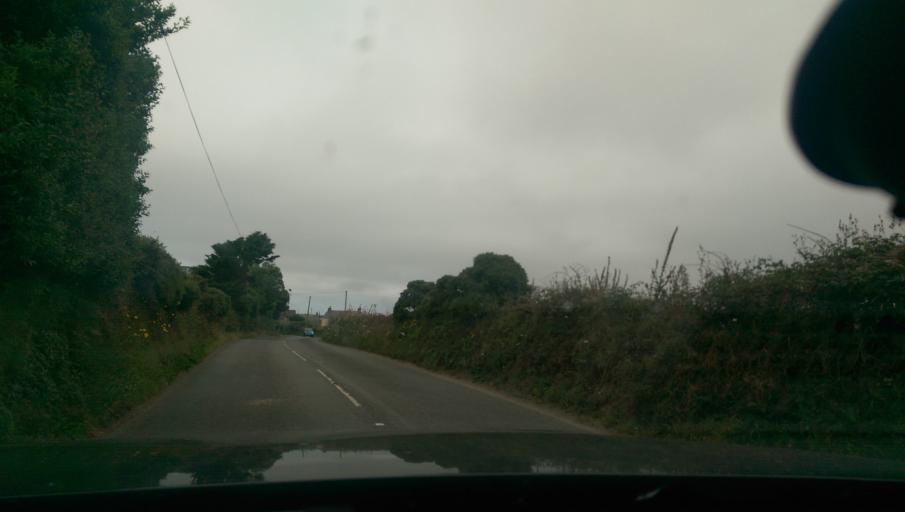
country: GB
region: England
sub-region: Cornwall
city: Saint Just
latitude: 50.1100
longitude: -5.6758
